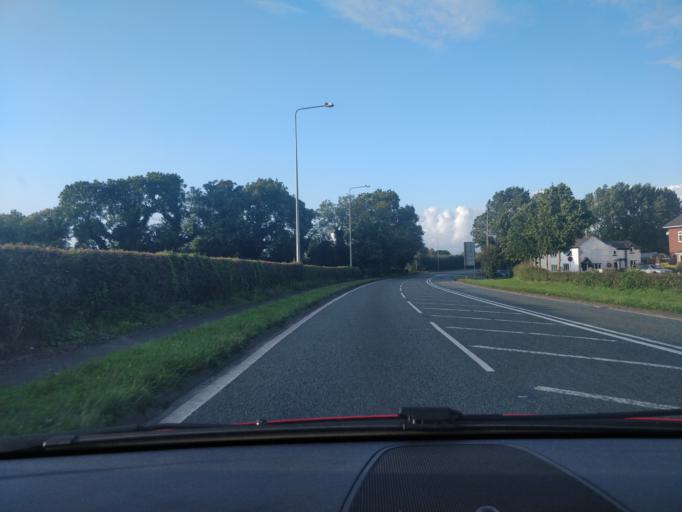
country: GB
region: England
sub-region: Lancashire
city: Tarleton
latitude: 53.6966
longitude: -2.8115
